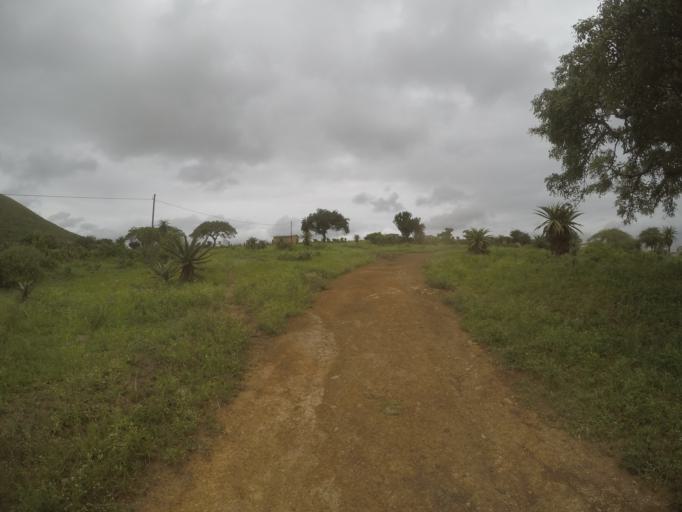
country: ZA
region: KwaZulu-Natal
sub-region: uThungulu District Municipality
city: Empangeni
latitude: -28.5984
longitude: 31.8498
